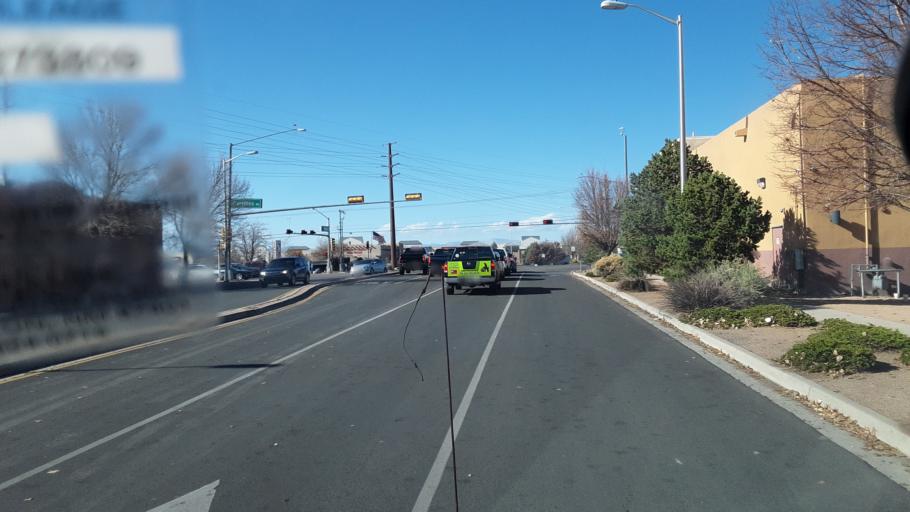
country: US
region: New Mexico
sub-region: Santa Fe County
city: Agua Fria
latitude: 35.6417
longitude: -106.0121
